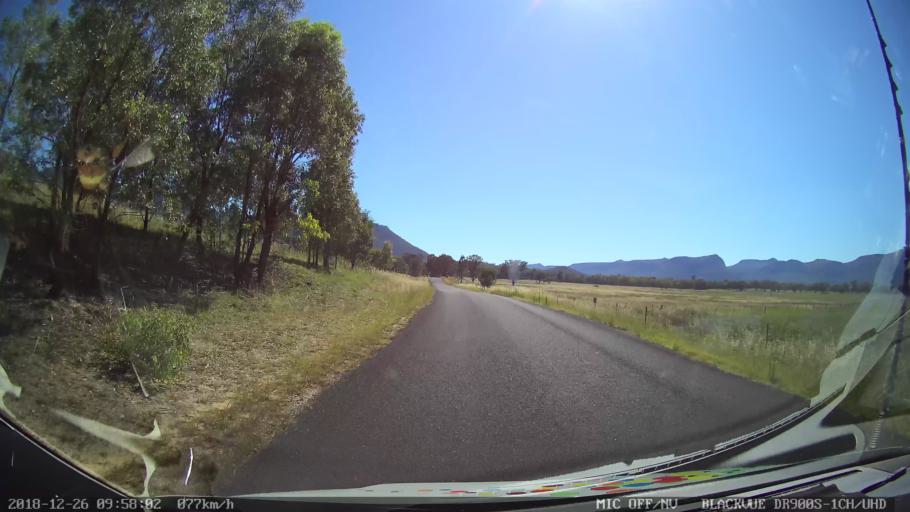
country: AU
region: New South Wales
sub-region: Mid-Western Regional
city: Kandos
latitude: -33.0402
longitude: 150.2002
